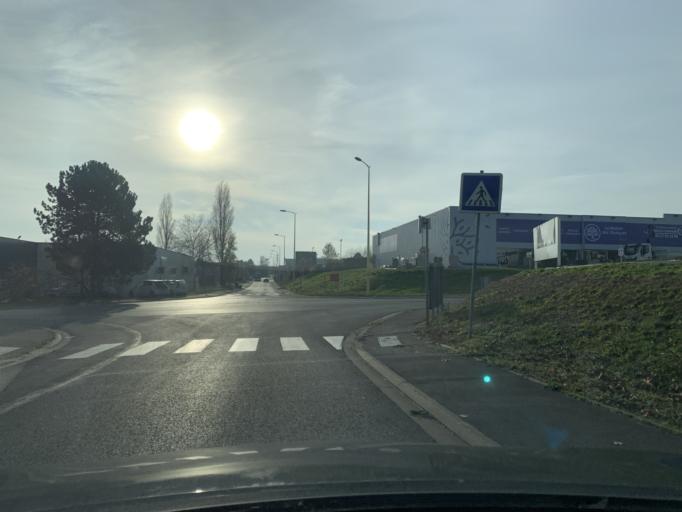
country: FR
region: Nord-Pas-de-Calais
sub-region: Departement du Nord
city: Proville
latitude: 50.1504
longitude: 3.2179
